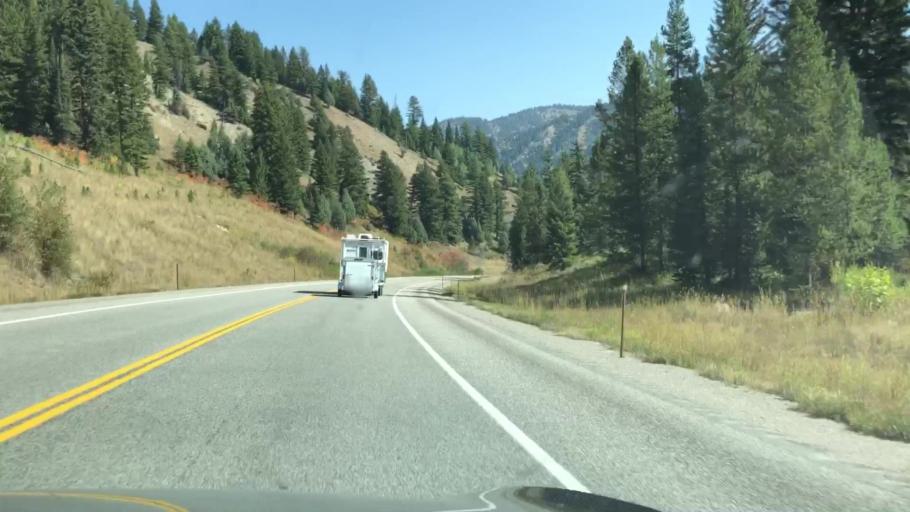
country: US
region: Wyoming
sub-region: Teton County
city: Hoback
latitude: 43.2288
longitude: -110.7842
